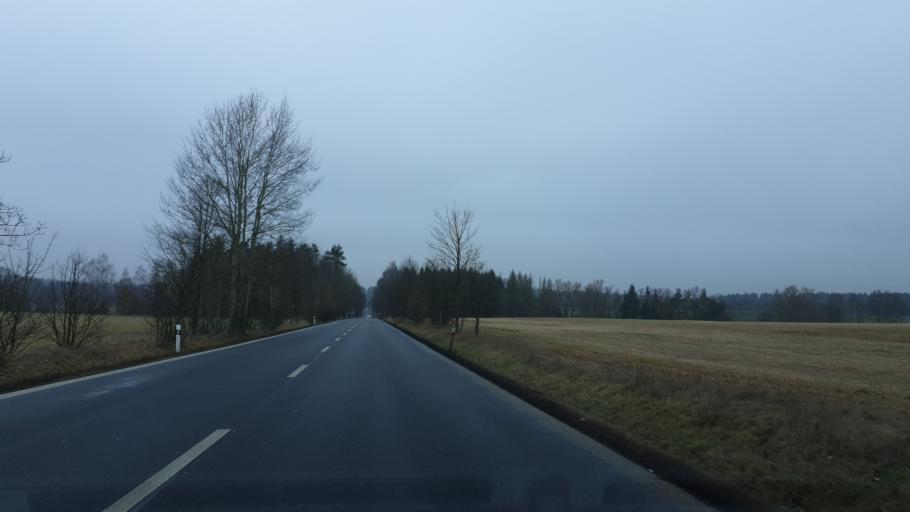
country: CZ
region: Karlovarsky
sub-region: Okres Cheb
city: Frantiskovy Lazne
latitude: 50.1351
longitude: 12.3386
